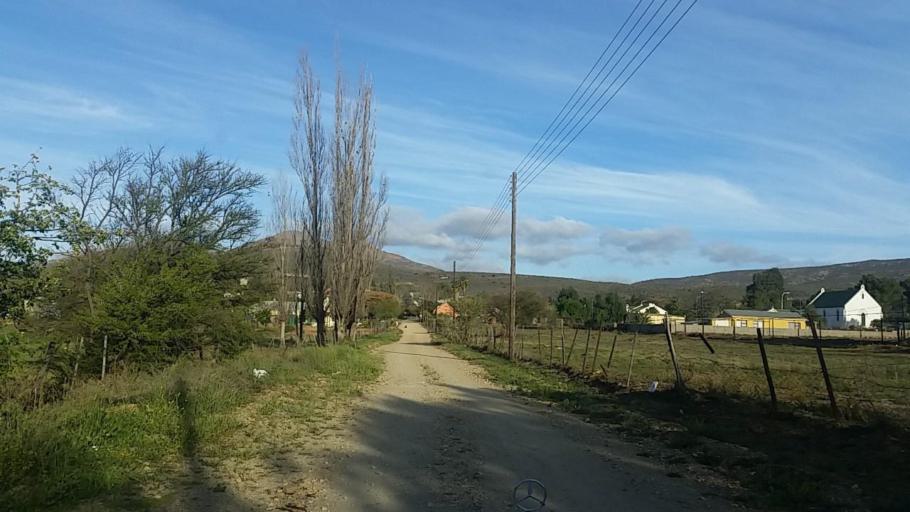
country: ZA
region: Western Cape
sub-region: Eden District Municipality
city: Knysna
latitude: -33.6574
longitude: 23.1190
